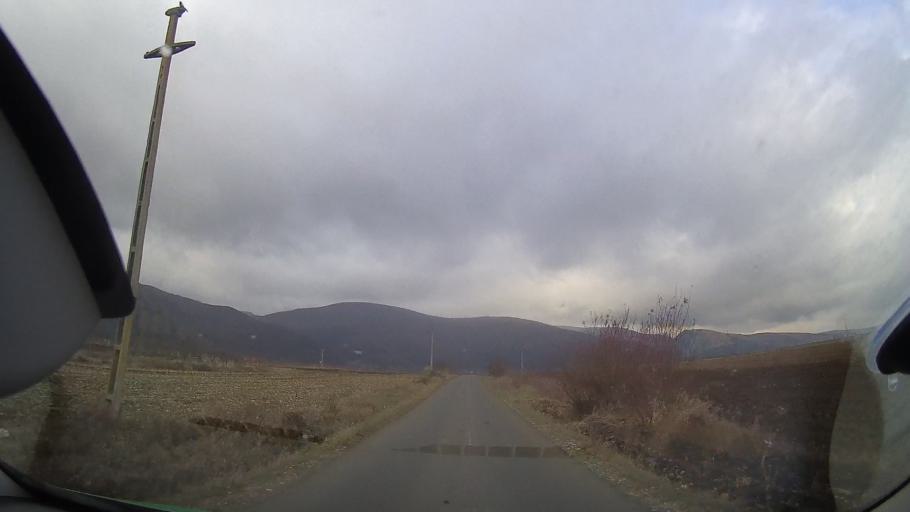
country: RO
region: Cluj
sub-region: Comuna Moldovenesti
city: Moldovenesti
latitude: 46.5060
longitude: 23.6743
